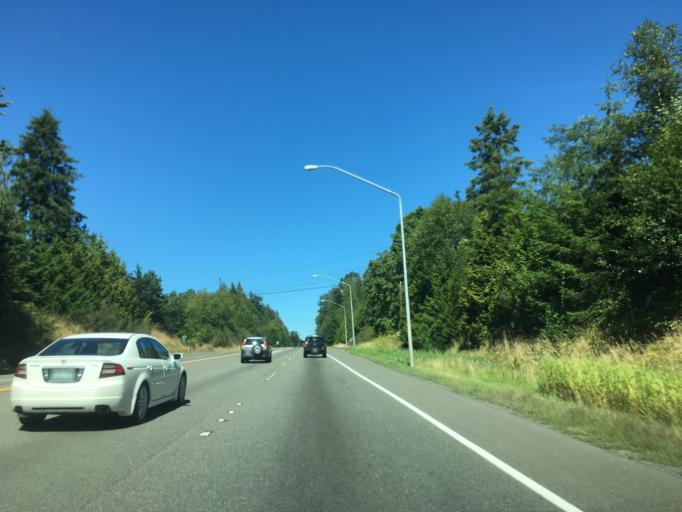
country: US
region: Washington
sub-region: Snohomish County
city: West Lake Stevens
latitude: 47.9940
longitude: -122.1229
